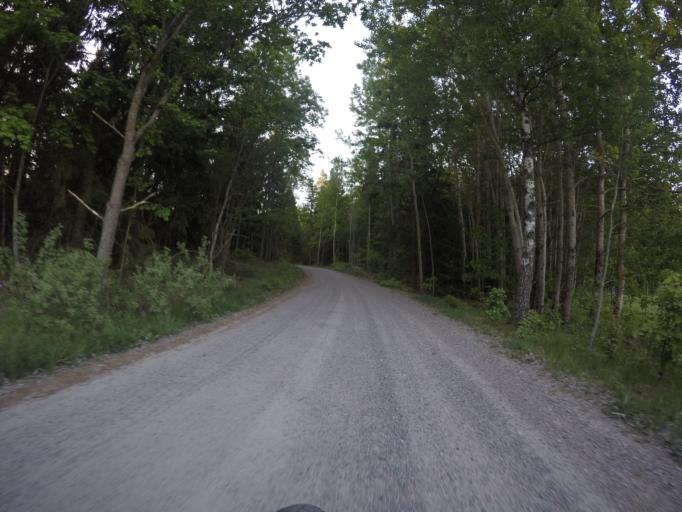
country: SE
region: Soedermanland
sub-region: Eskilstuna Kommun
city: Skogstorp
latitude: 59.3308
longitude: 16.4921
